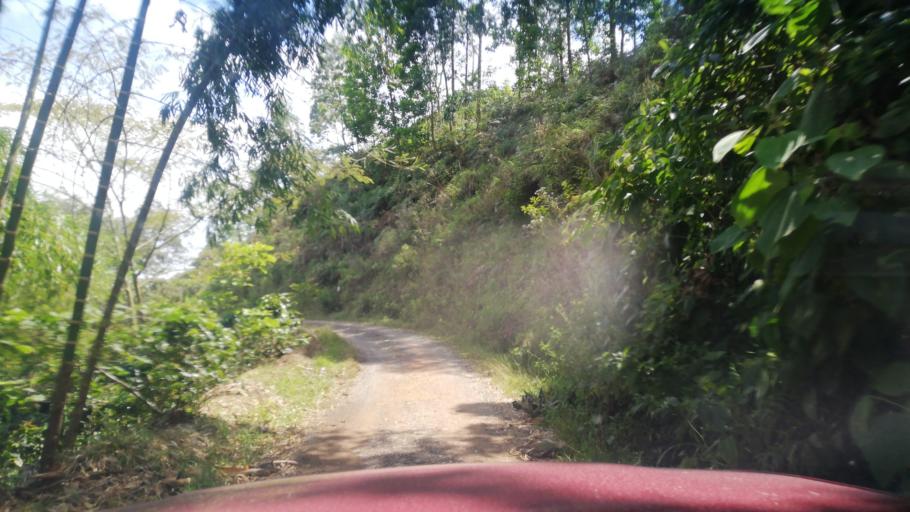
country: CO
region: Risaralda
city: Balboa
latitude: 4.9319
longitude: -75.9655
